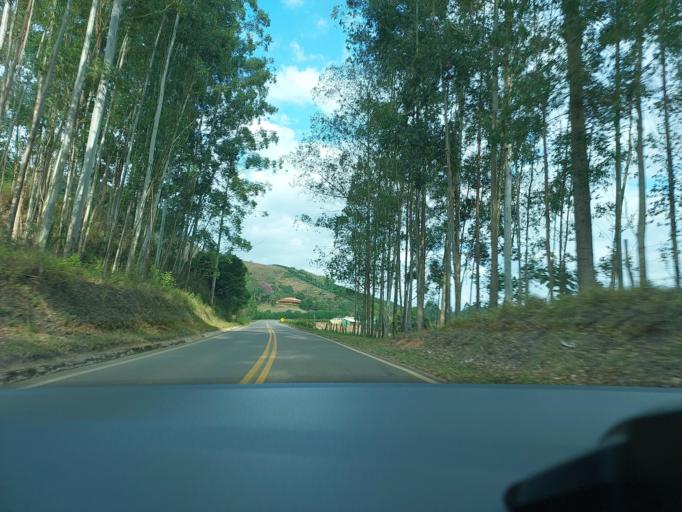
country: BR
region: Minas Gerais
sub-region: Visconde Do Rio Branco
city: Visconde do Rio Branco
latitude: -20.8853
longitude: -42.6608
